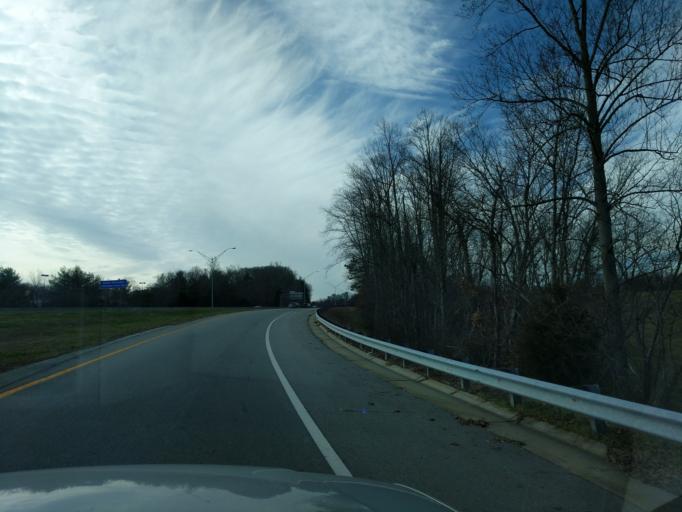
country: US
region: North Carolina
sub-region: Buncombe County
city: Bent Creek
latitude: 35.5606
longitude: -82.6398
